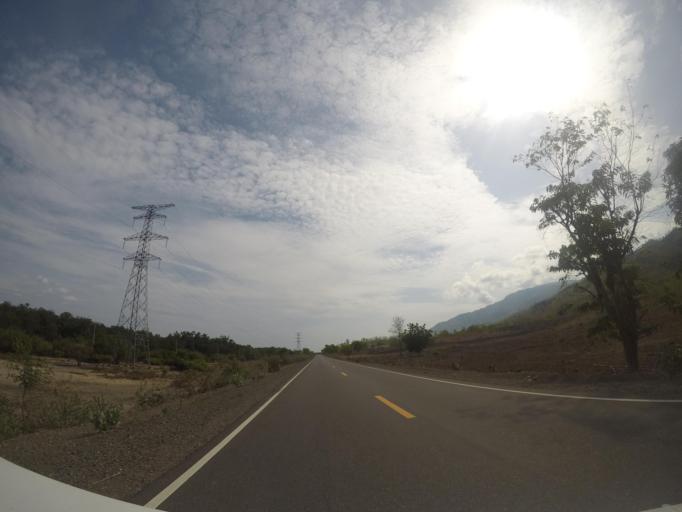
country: ID
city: Metinaro
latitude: -8.5048
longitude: 125.8095
